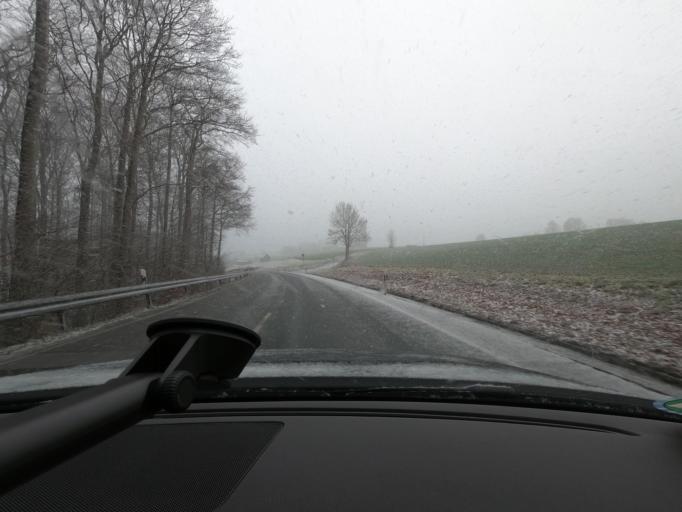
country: DE
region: North Rhine-Westphalia
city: Marsberg
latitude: 51.5093
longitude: 8.8716
